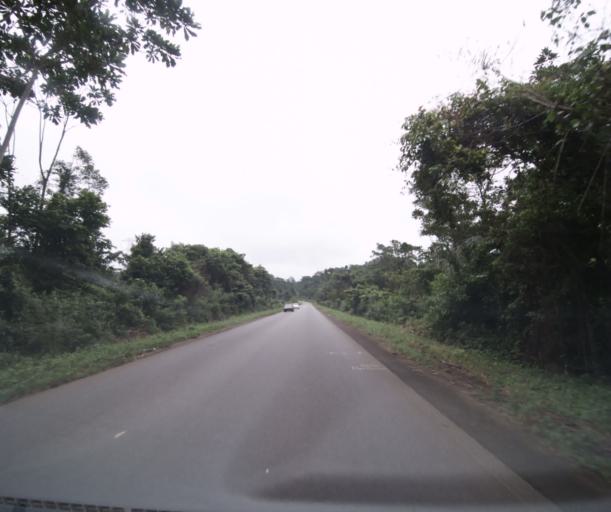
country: CM
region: Littoral
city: Edea
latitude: 3.6702
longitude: 10.1109
